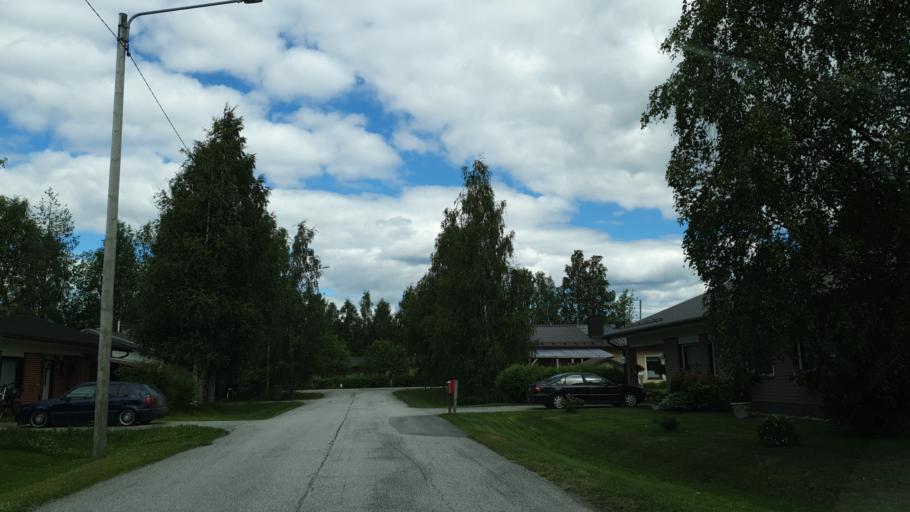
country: FI
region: Kainuu
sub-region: Kehys-Kainuu
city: Kuhmo
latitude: 64.1157
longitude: 29.4804
